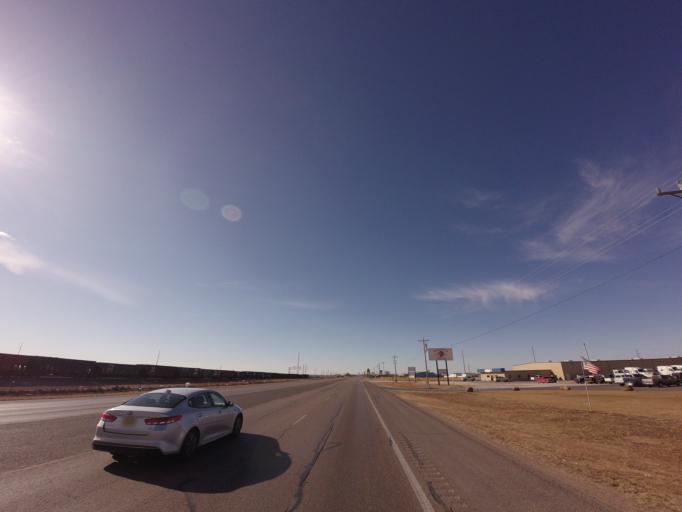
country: US
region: New Mexico
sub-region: Curry County
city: Clovis
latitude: 34.3937
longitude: -103.1371
